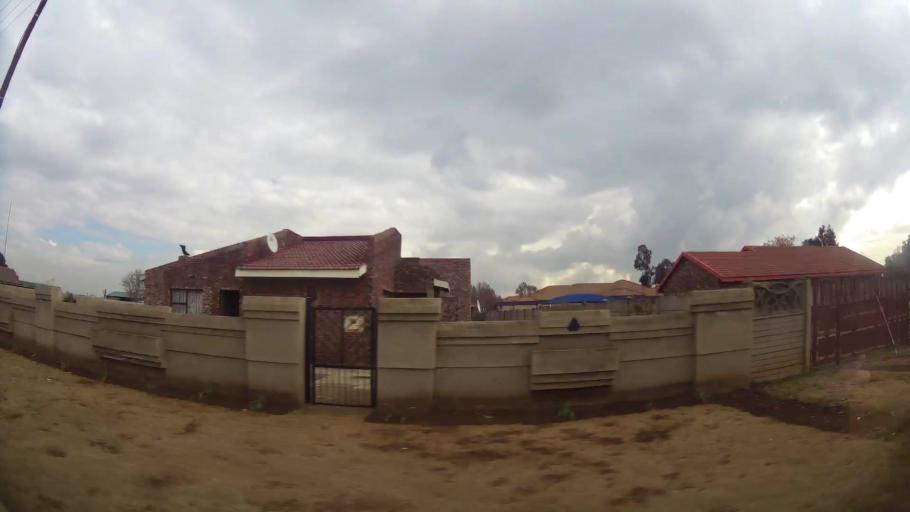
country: ZA
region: Gauteng
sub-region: Sedibeng District Municipality
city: Meyerton
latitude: -26.5869
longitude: 27.9998
